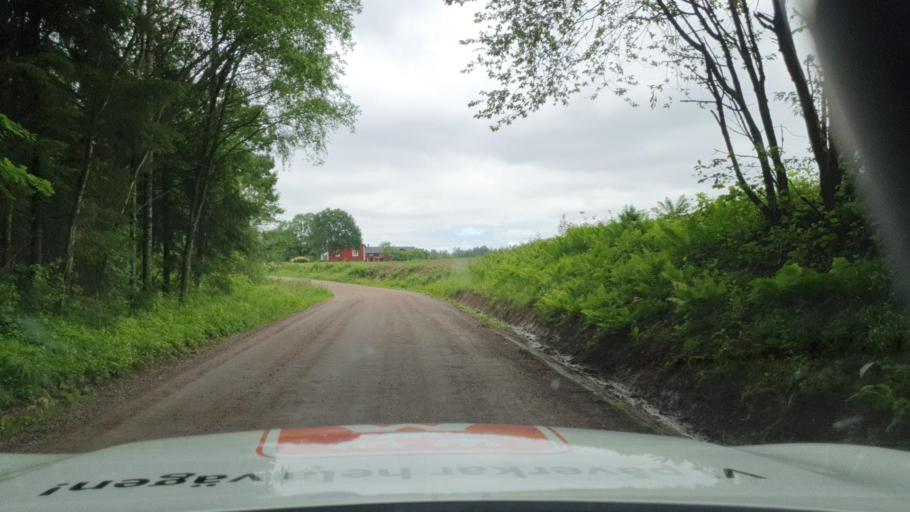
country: SE
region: Vaermland
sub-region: Filipstads Kommun
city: Filipstad
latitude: 59.5561
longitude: 13.9790
